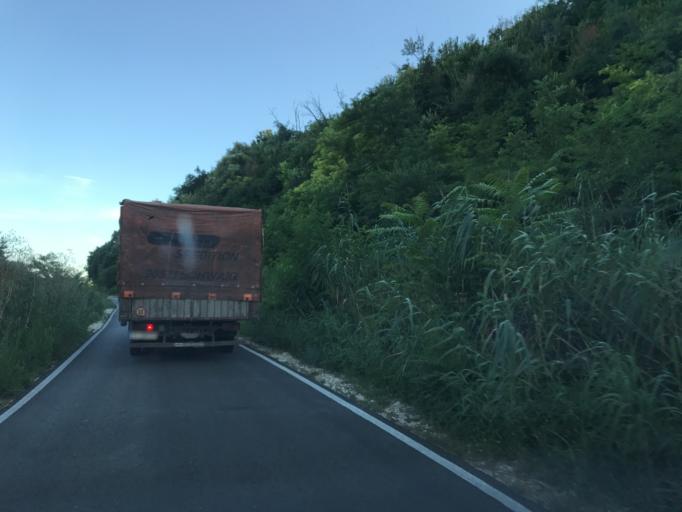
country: BG
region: Vidin
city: Bregovo
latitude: 44.1372
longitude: 22.6025
